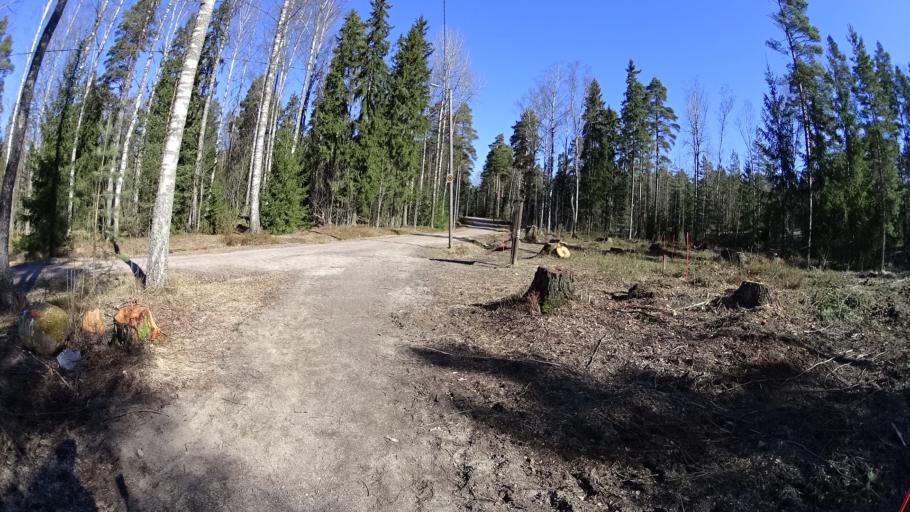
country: FI
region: Uusimaa
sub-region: Helsinki
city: Kilo
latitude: 60.2273
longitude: 24.8013
